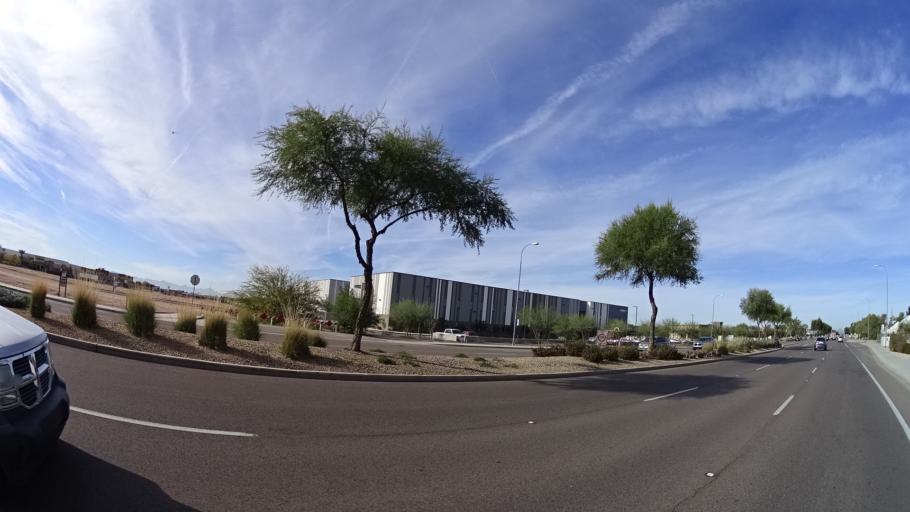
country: US
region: Arizona
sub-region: Maricopa County
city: Chandler
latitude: 33.2730
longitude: -111.7896
